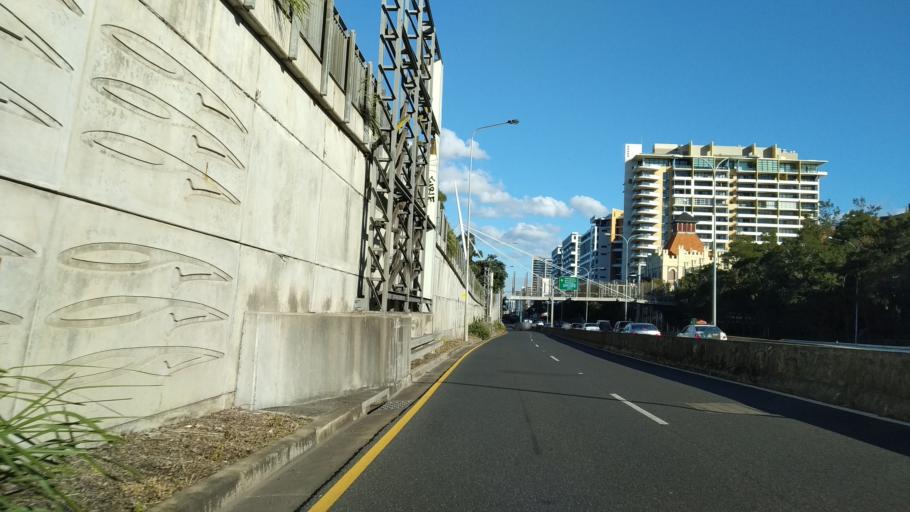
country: AU
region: New South Wales
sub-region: City of Sydney
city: Redfern
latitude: -33.8954
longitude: 151.2164
